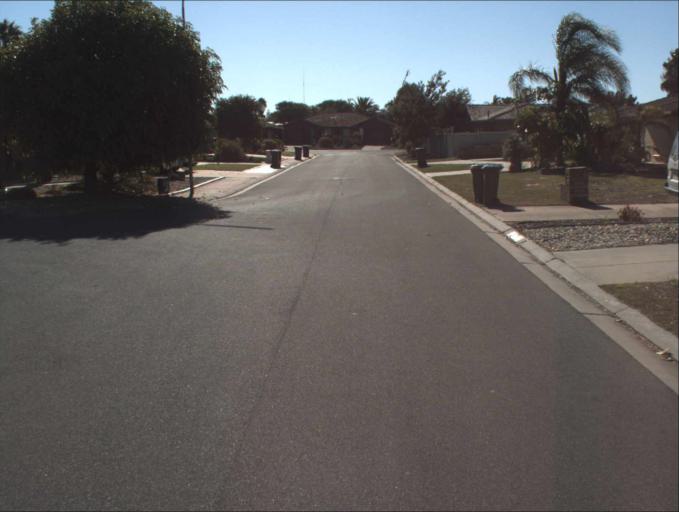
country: AU
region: South Australia
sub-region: Port Adelaide Enfield
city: Birkenhead
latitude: -34.7823
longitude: 138.4944
